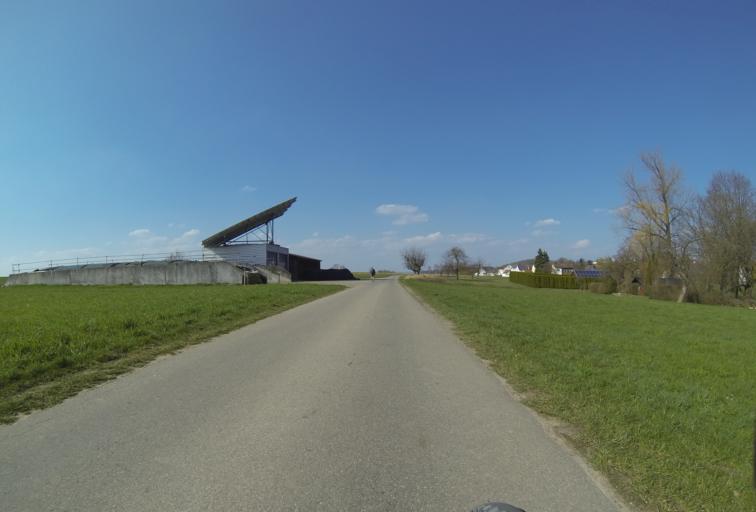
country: DE
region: Baden-Wuerttemberg
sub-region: Tuebingen Region
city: Huttisheim
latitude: 48.2575
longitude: 9.9524
